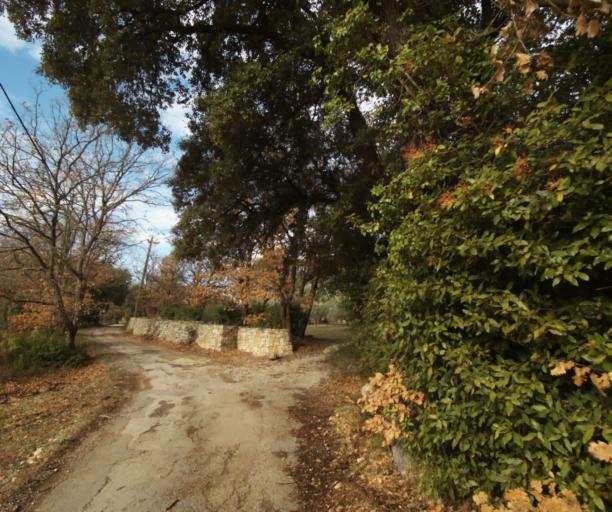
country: FR
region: Provence-Alpes-Cote d'Azur
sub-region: Departement du Var
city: Trans-en-Provence
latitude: 43.5057
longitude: 6.4762
